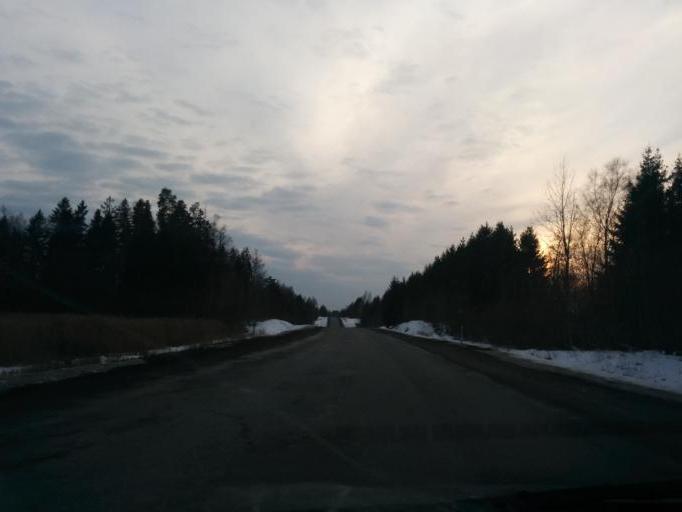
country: LV
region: Priekuli
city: Priekuli
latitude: 57.2775
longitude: 25.4842
